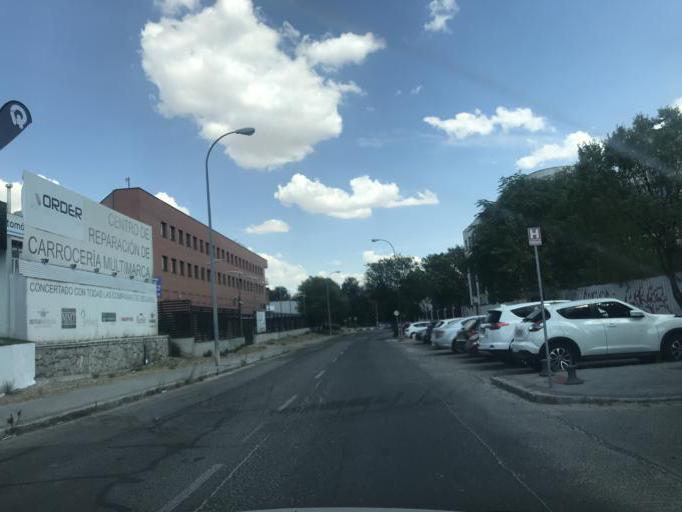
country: ES
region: Madrid
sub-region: Provincia de Madrid
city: Alcobendas
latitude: 40.5352
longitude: -3.6466
